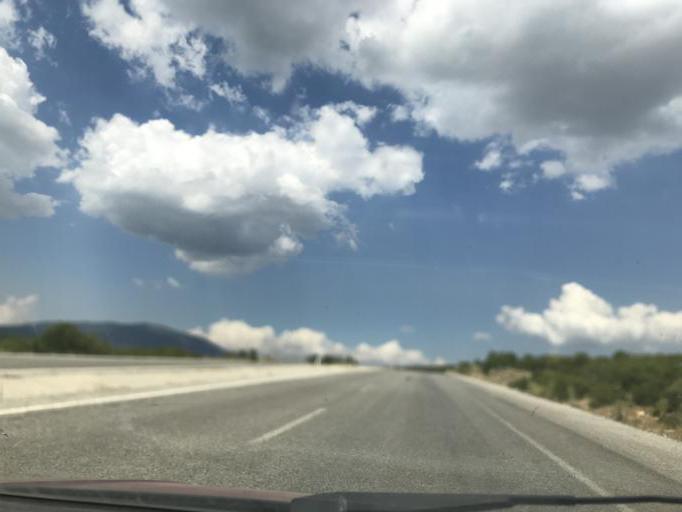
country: TR
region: Denizli
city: Tavas
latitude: 37.5880
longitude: 29.1050
